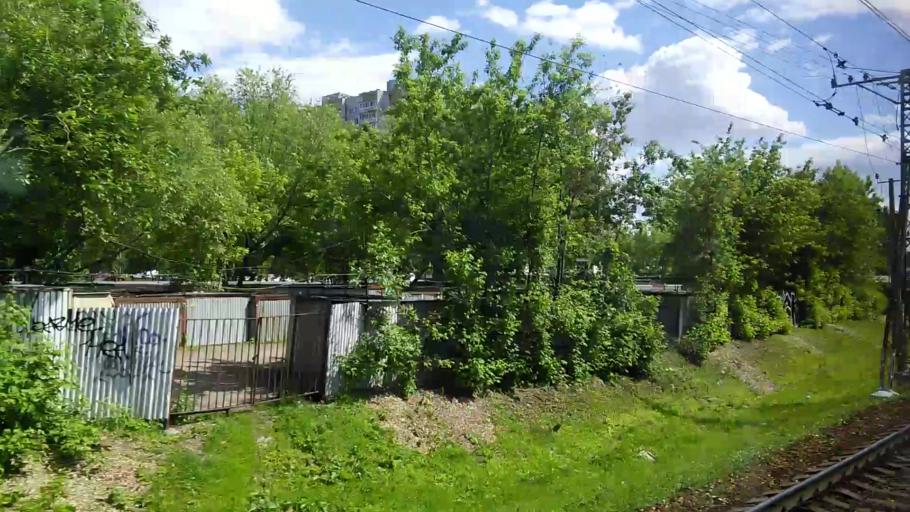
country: RU
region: Moscow
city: Likhobory
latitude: 55.8228
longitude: 37.5741
